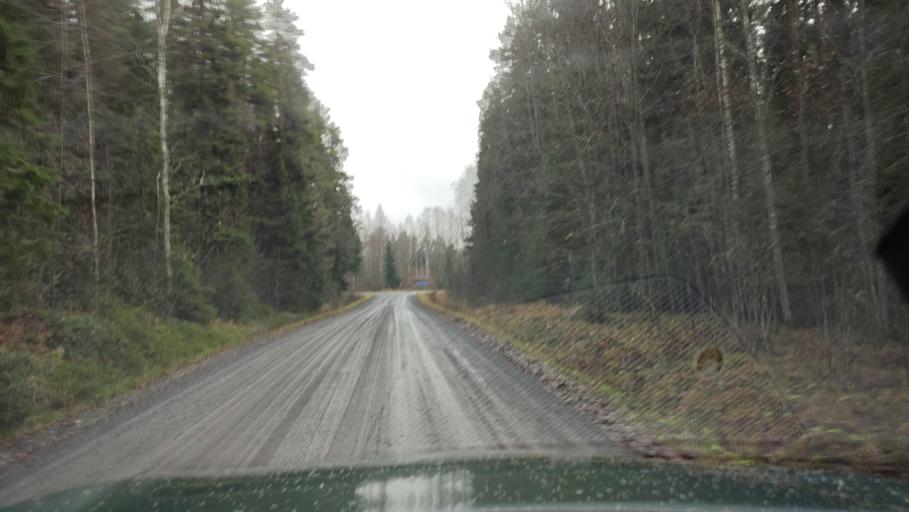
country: FI
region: Ostrobothnia
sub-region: Sydosterbotten
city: Naerpes
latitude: 62.4596
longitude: 21.4919
